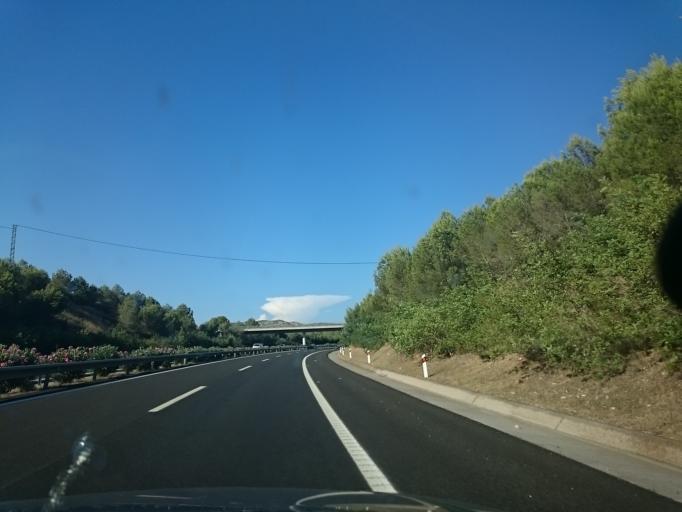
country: ES
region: Catalonia
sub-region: Provincia de Barcelona
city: Cubelles
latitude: 41.2402
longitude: 1.6833
